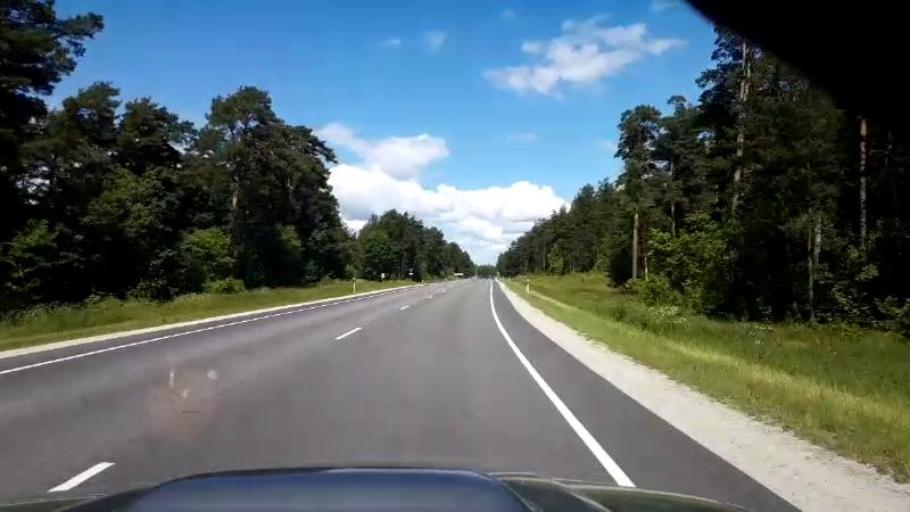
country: EE
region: Paernumaa
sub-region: Paernu linn
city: Parnu
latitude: 58.2036
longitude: 24.4855
